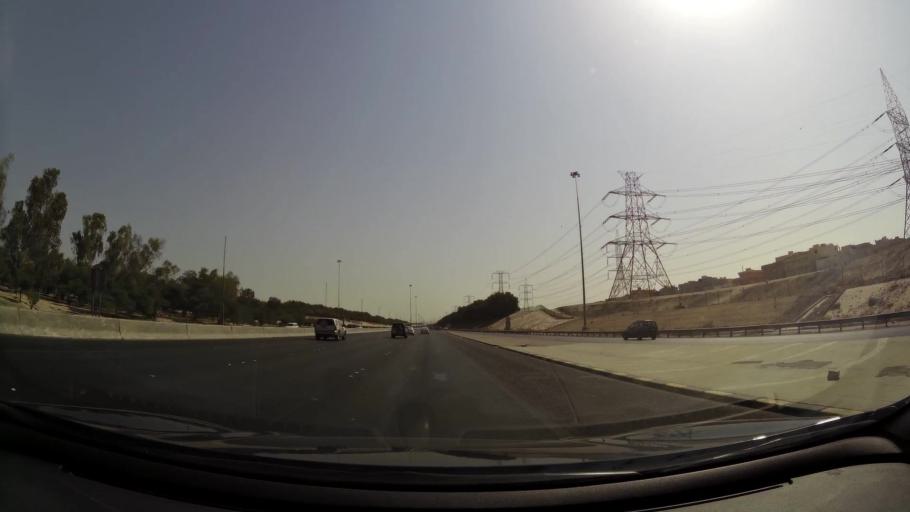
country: KW
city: Bayan
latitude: 29.3039
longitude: 48.0233
